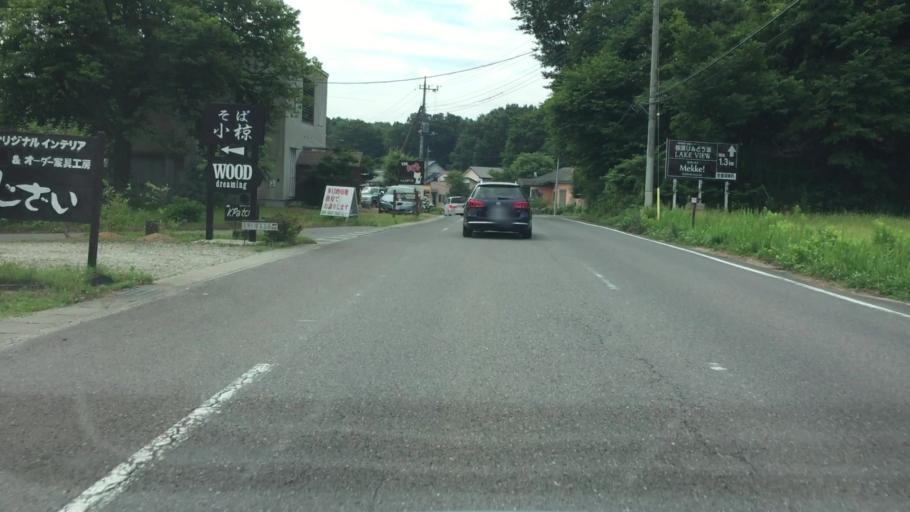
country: JP
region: Tochigi
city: Kuroiso
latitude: 37.0508
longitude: 140.0377
